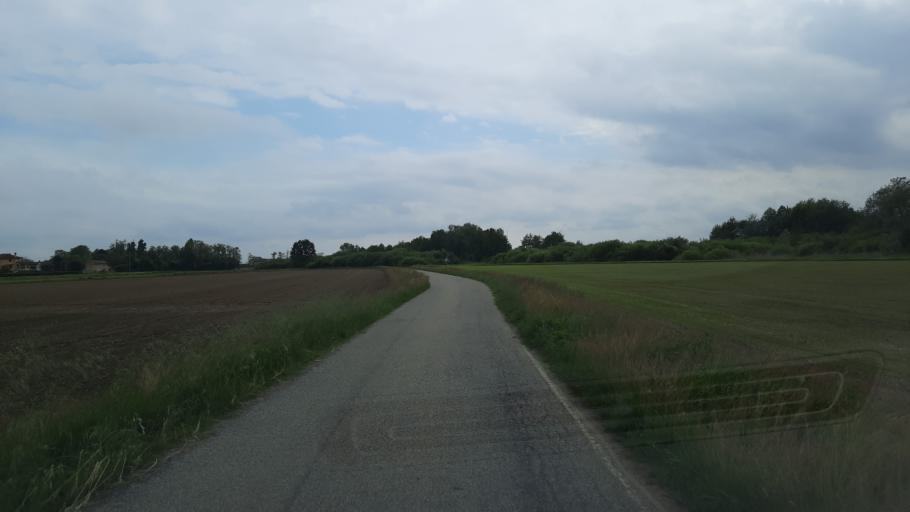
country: IT
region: Lombardy
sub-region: Provincia di Pavia
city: Castelnovetto
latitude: 45.2332
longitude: 8.6032
